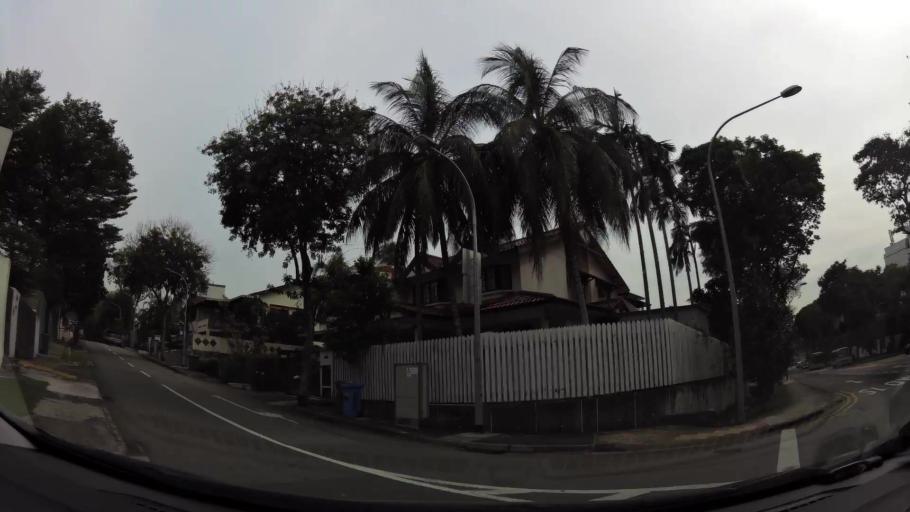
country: SG
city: Singapore
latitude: 1.3271
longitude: 103.7936
